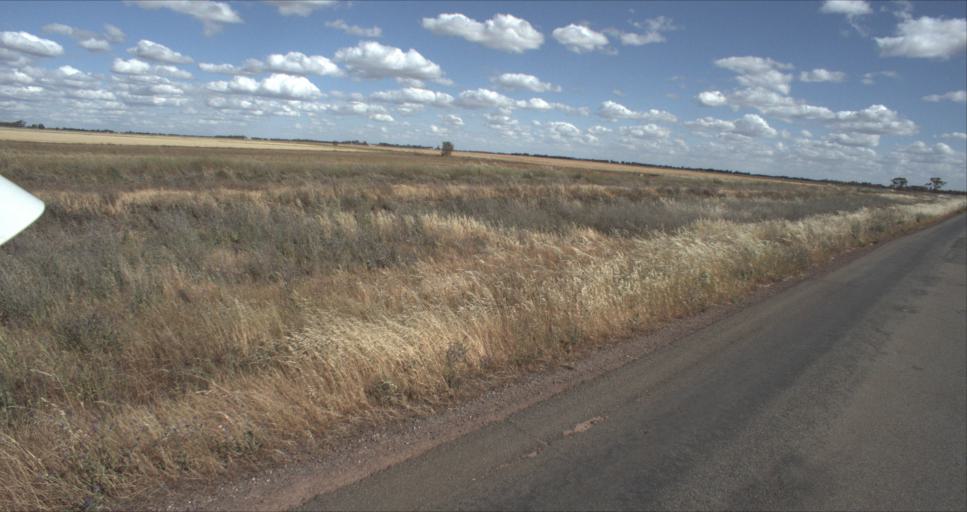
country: AU
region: New South Wales
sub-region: Leeton
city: Leeton
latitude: -34.4224
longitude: 146.2639
